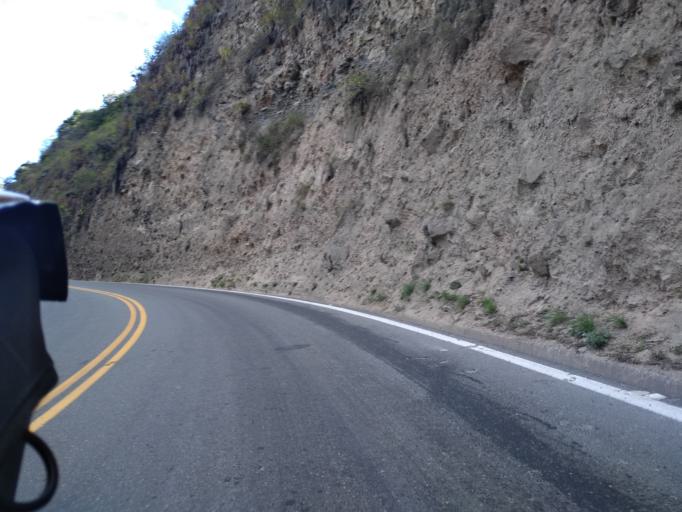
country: CO
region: Narino
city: Imues
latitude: 1.0542
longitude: -77.4506
